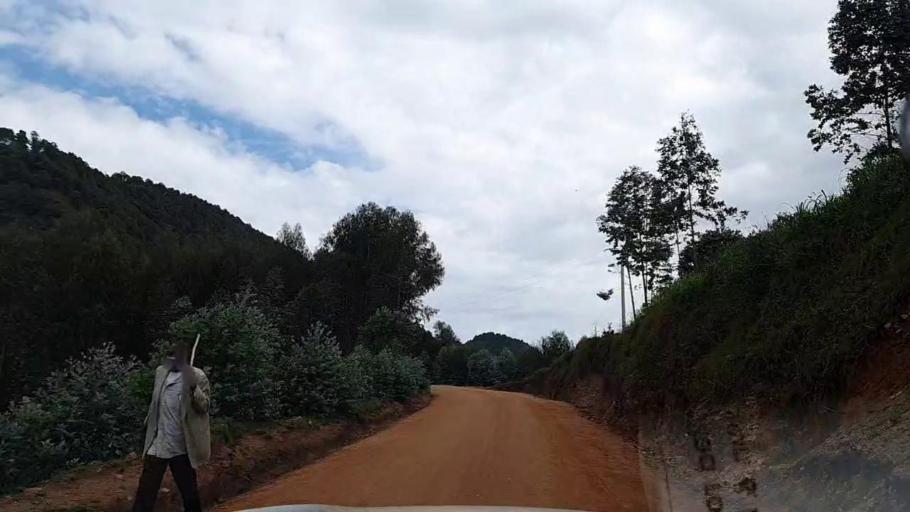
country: RW
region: Southern Province
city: Nzega
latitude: -2.3956
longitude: 29.4523
